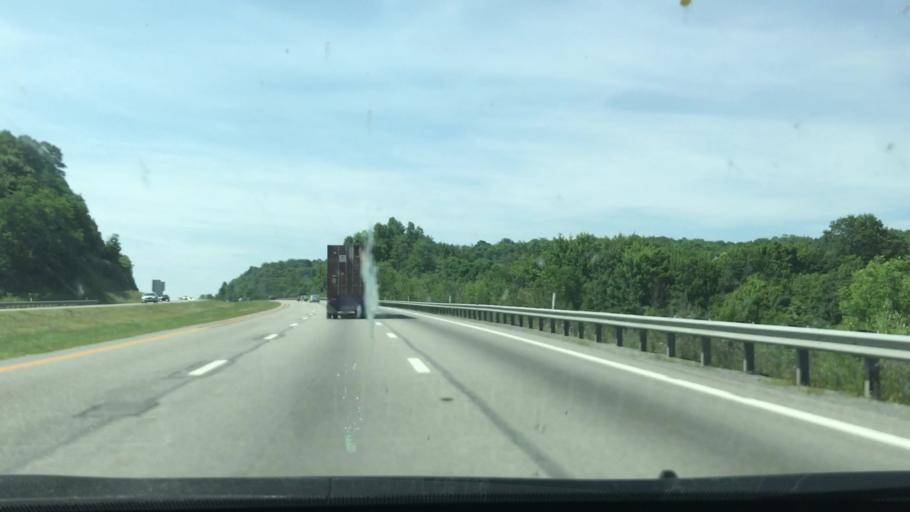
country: US
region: West Virginia
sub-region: Raleigh County
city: Shady Spring
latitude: 37.5982
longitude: -81.1274
